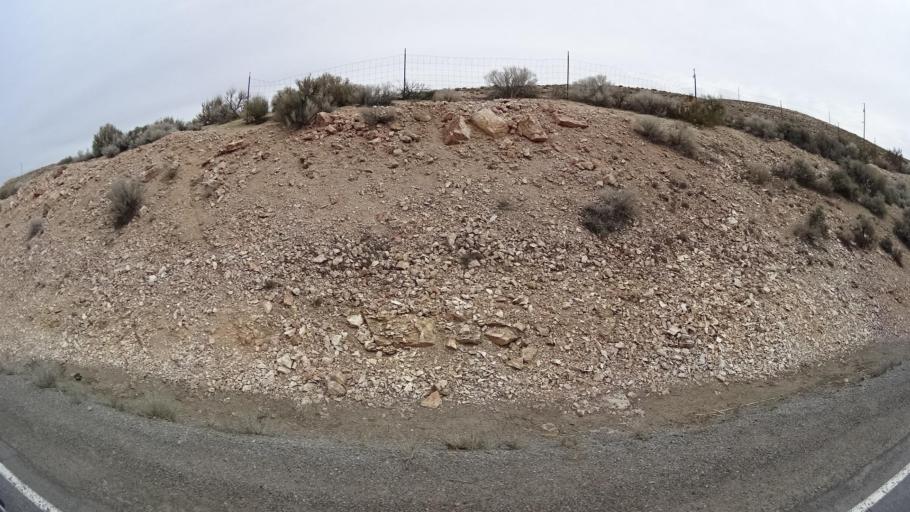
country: US
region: Nevada
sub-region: Washoe County
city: Golden Valley
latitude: 39.6063
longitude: -119.8109
